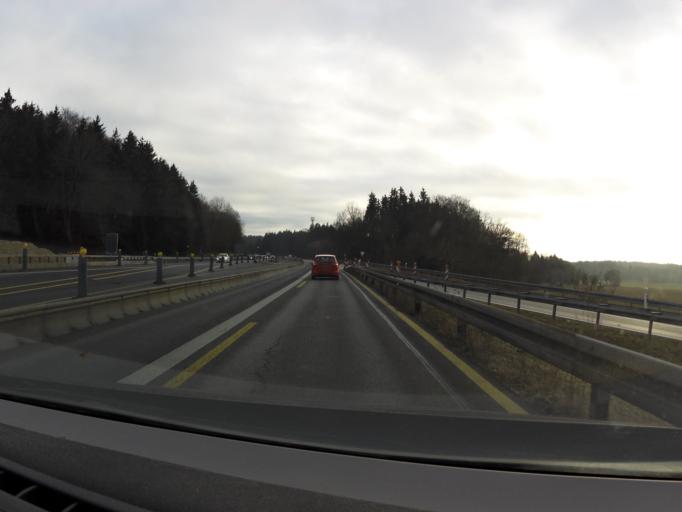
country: DE
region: Bavaria
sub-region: Upper Bavaria
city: Schaftlarn
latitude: 48.0142
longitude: 11.4172
